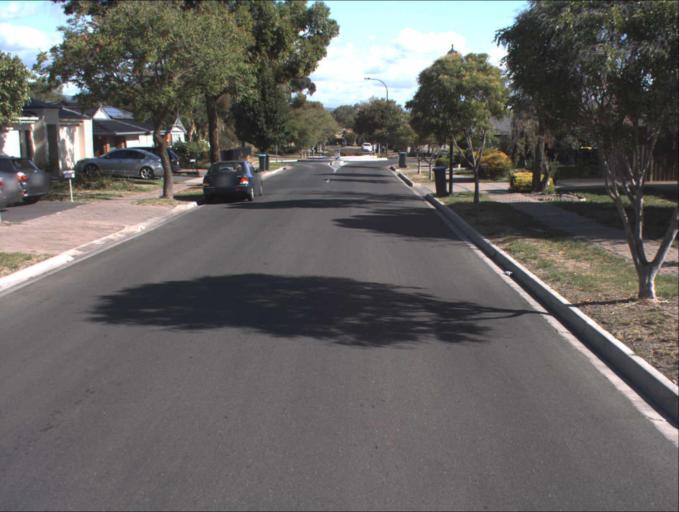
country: AU
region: South Australia
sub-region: Port Adelaide Enfield
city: Gilles Plains
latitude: -34.8599
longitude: 138.6396
